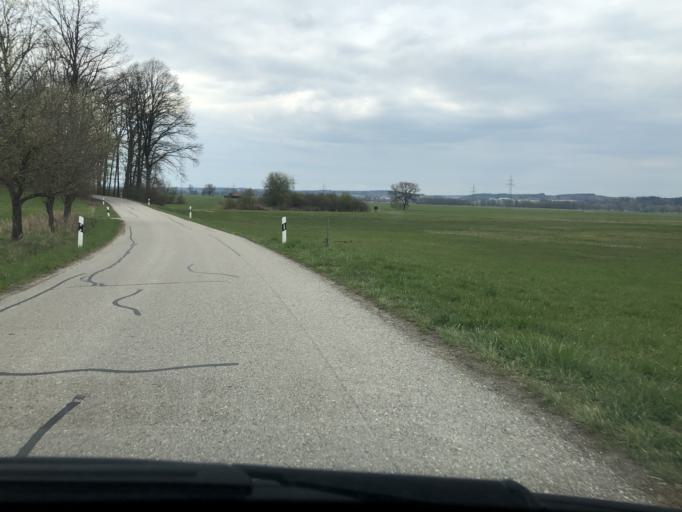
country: DE
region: Bavaria
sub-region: Upper Bavaria
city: Zolling
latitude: 48.4409
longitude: 11.7337
